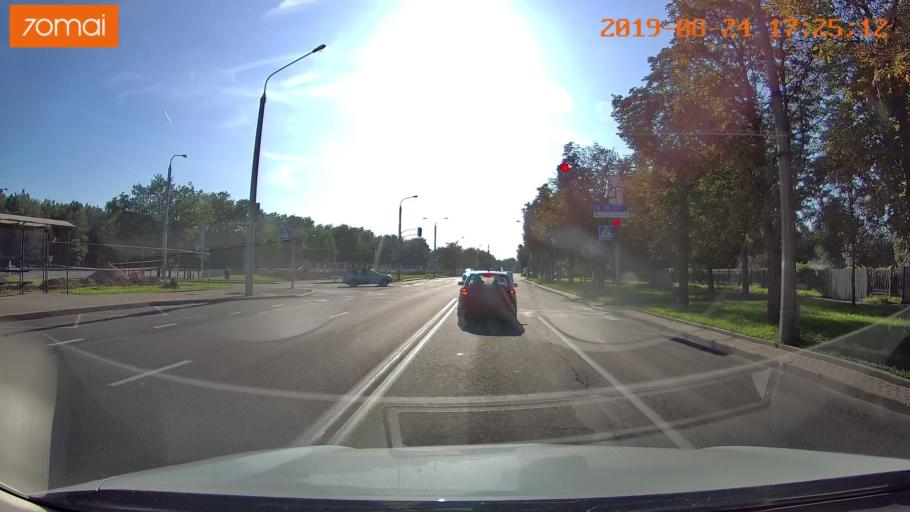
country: BY
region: Minsk
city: Hatava
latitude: 53.8348
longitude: 27.6448
